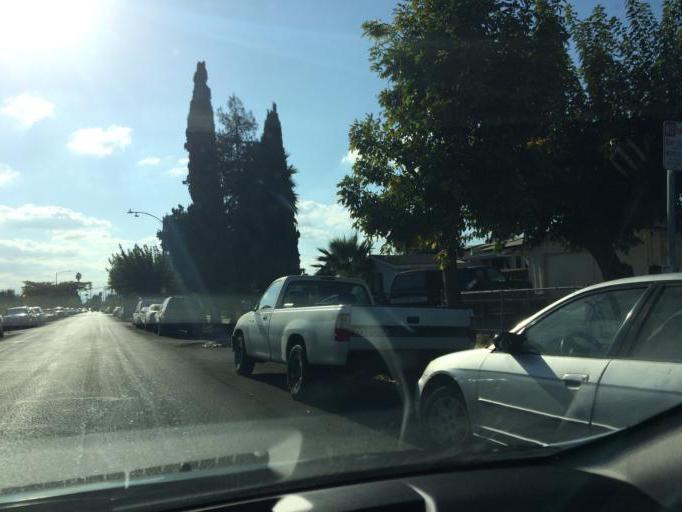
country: US
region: California
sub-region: Santa Clara County
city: Alum Rock
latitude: 37.3289
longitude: -121.8246
